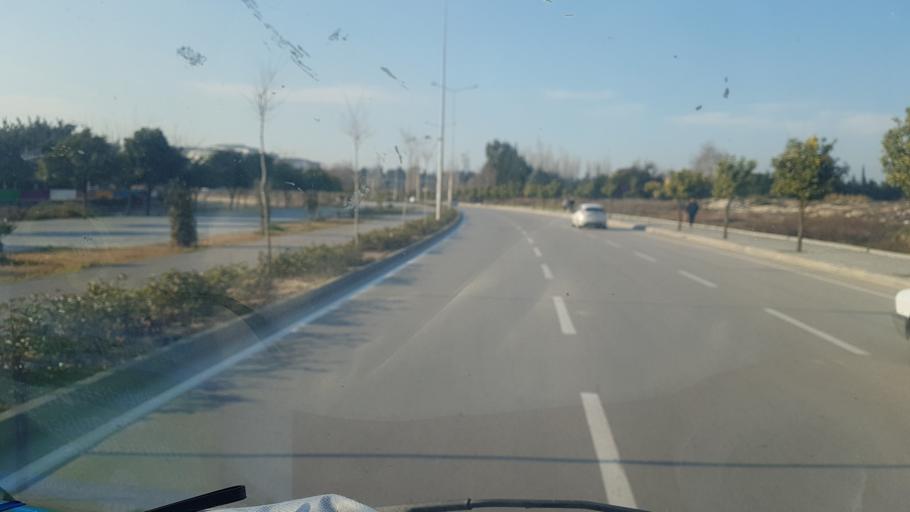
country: TR
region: Adana
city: Adana
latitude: 37.0106
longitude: 35.3527
